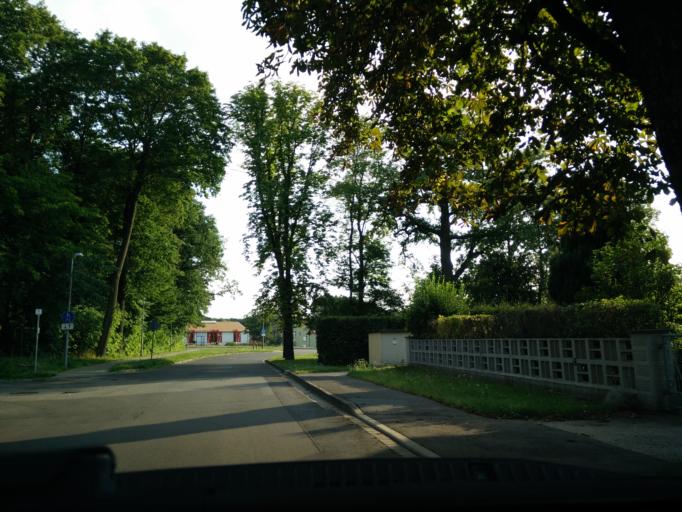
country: DE
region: Saxony
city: Frohburg
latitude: 51.0670
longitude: 12.5580
